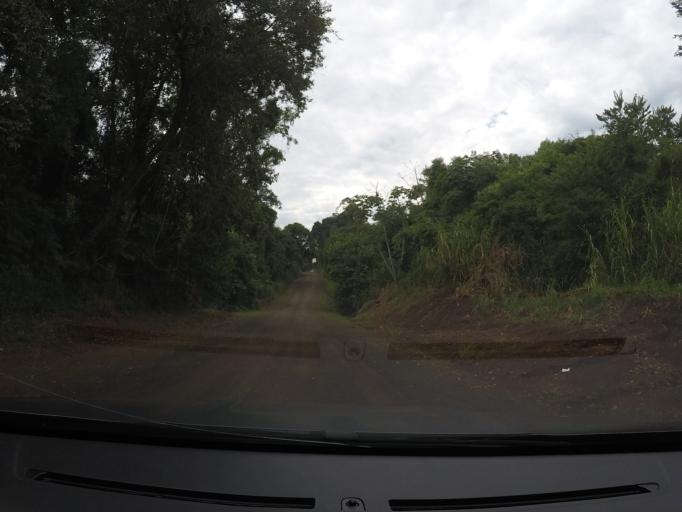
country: AR
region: Misiones
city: Puerto Rico
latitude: -26.8111
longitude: -55.0318
